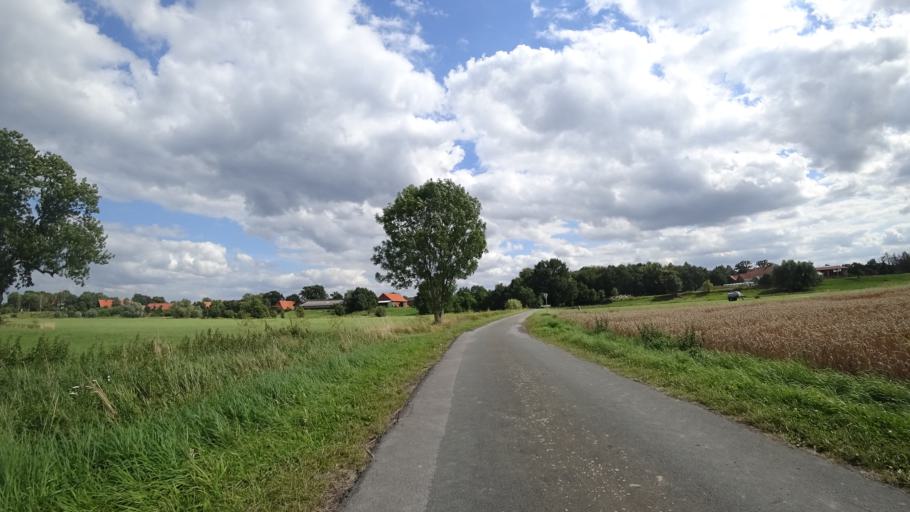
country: DE
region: Lower Saxony
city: Stolzenau
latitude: 52.4674
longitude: 9.0467
